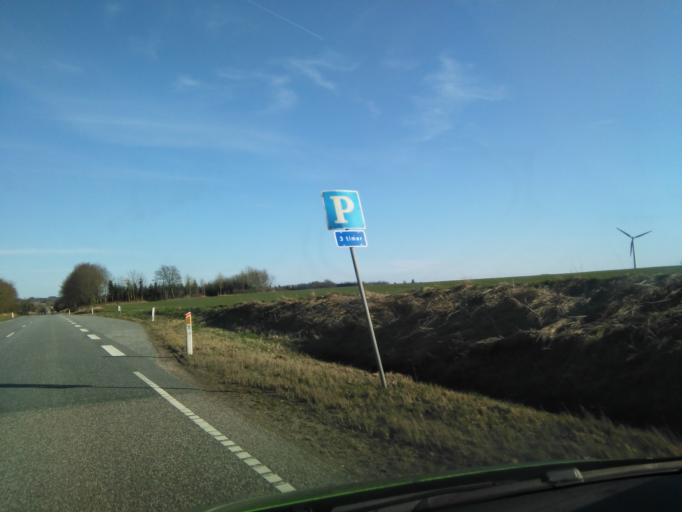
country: DK
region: Central Jutland
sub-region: Horsens Kommune
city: Braedstrup
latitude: 55.9065
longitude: 9.5942
